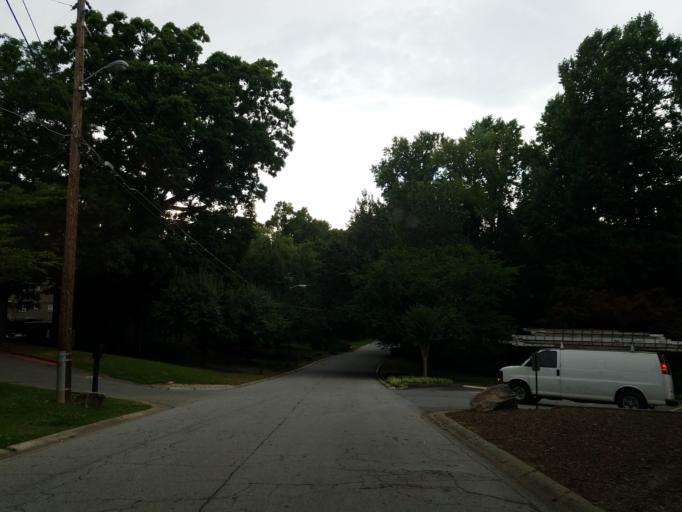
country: US
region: Georgia
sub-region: Cobb County
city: Marietta
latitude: 33.9389
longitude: -84.5473
